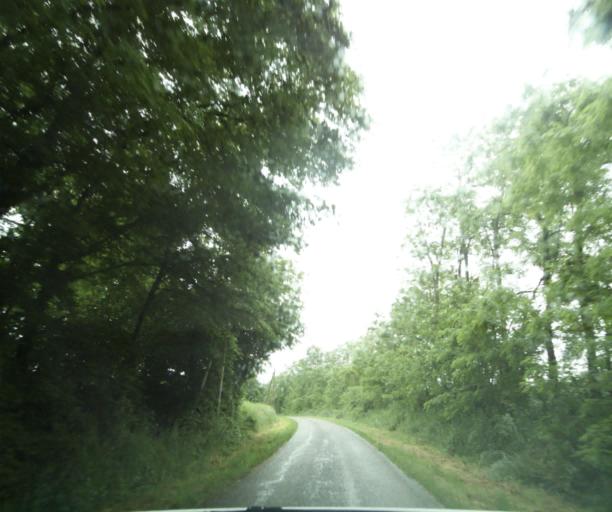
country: FR
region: Bourgogne
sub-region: Departement de Saone-et-Loire
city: Palinges
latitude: 46.4737
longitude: 4.2066
